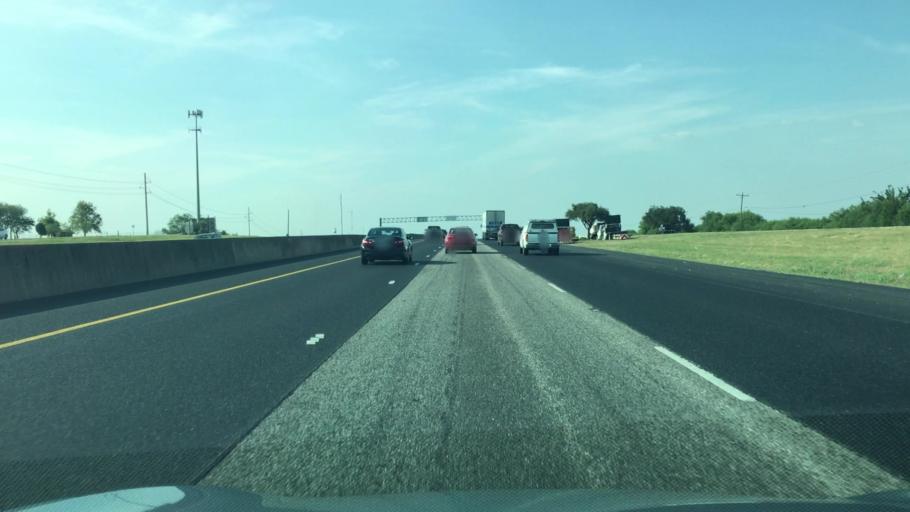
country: US
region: Texas
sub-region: Hays County
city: Kyle
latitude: 29.9728
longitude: -97.8745
